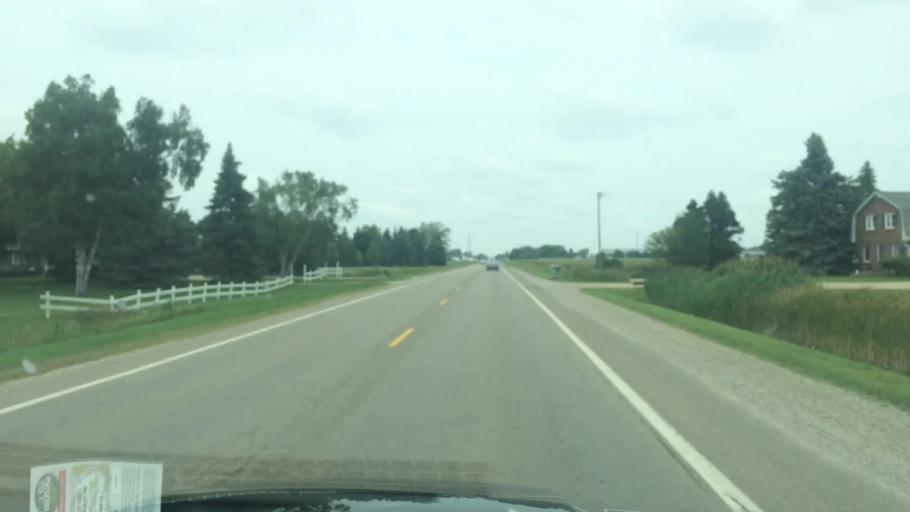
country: US
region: Michigan
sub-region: Huron County
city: Bad Axe
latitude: 43.8300
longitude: -83.0012
